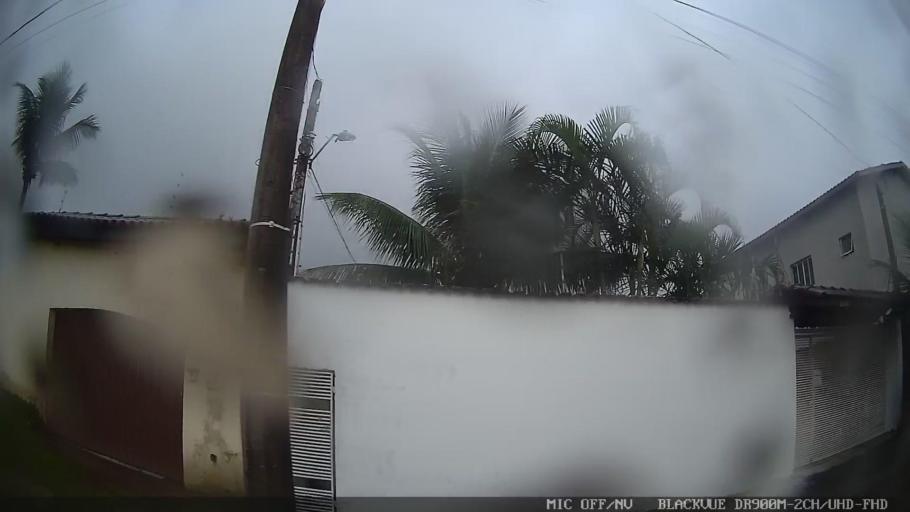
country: BR
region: Sao Paulo
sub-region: Itanhaem
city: Itanhaem
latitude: -24.2008
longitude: -46.8302
